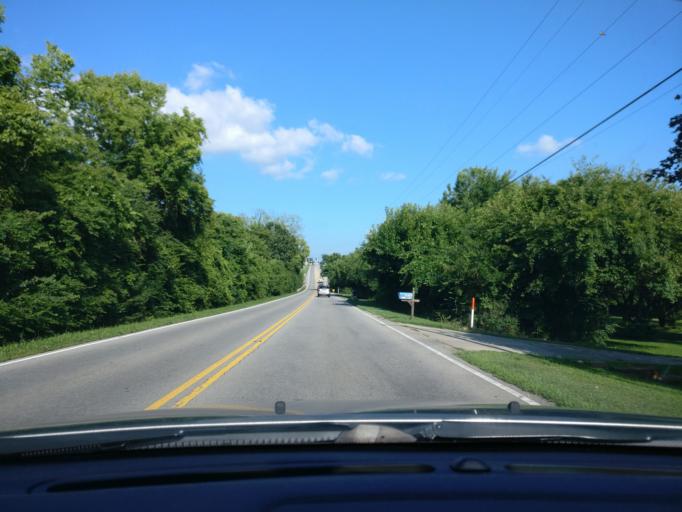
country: US
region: Ohio
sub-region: Warren County
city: Springboro
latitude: 39.5509
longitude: -84.2157
